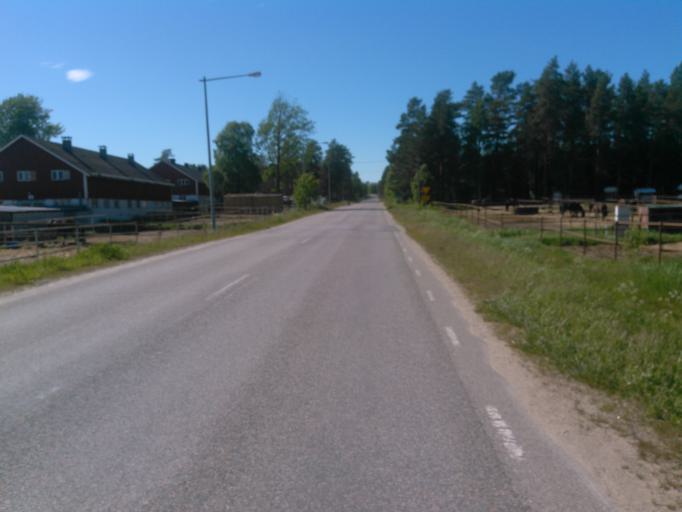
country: SE
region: Vaesterbotten
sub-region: Umea Kommun
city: Roback
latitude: 63.8237
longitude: 20.1810
